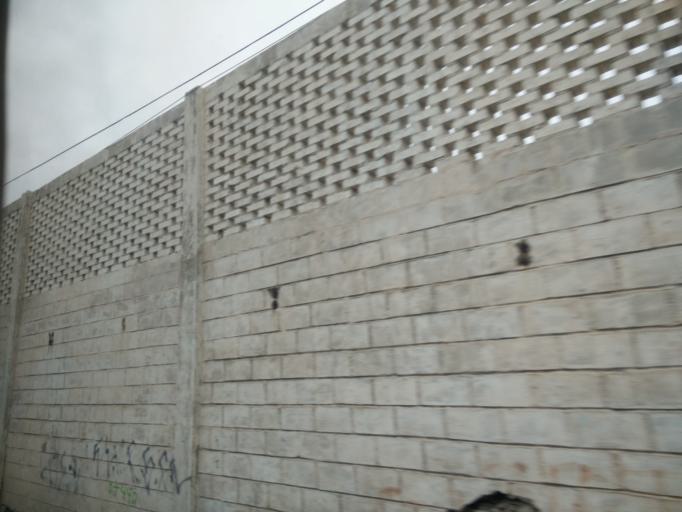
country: MX
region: Sonora
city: Heroica Guaymas
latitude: 27.9245
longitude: -110.9114
